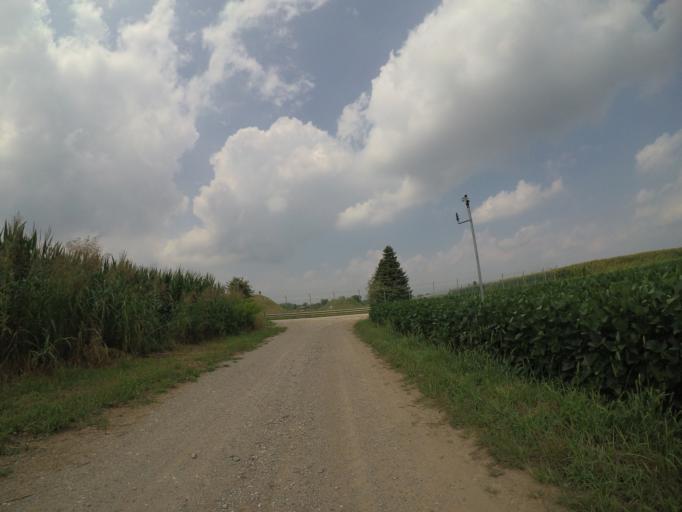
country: IT
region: Friuli Venezia Giulia
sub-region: Provincia di Udine
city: Codroipo
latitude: 45.9844
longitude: 12.9992
